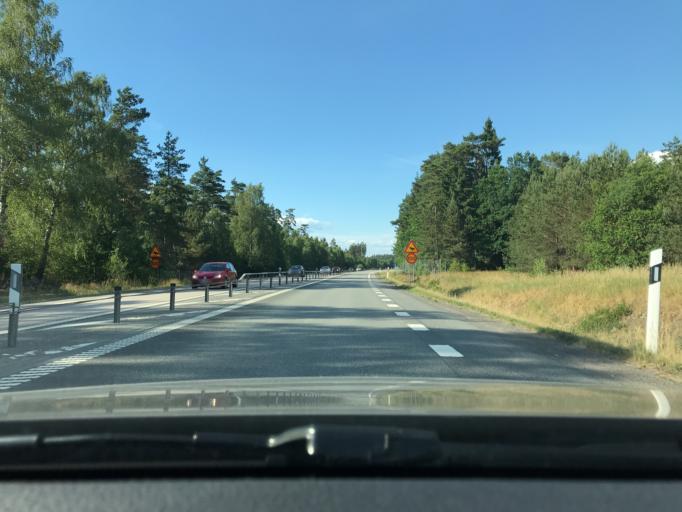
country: SE
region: Skane
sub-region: Osby Kommun
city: Osby
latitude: 56.3943
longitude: 14.0370
